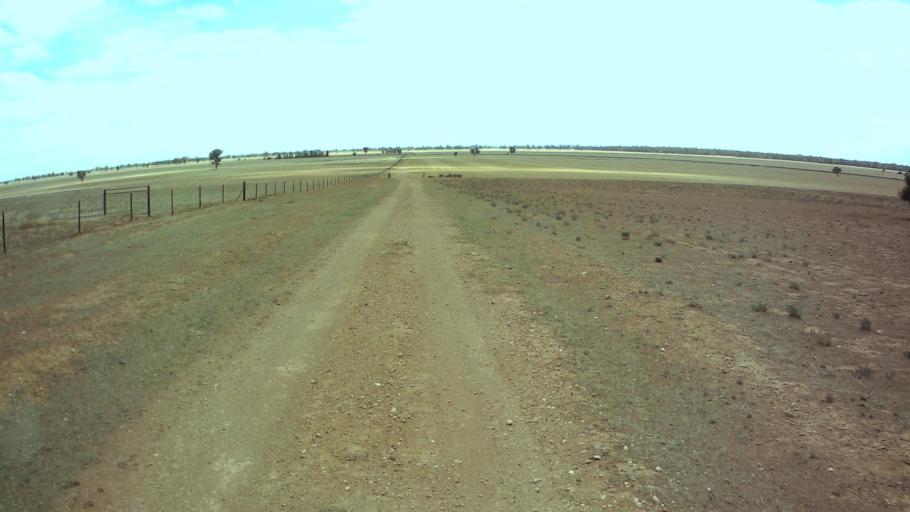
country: AU
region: New South Wales
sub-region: Weddin
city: Grenfell
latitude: -33.9029
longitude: 147.7385
